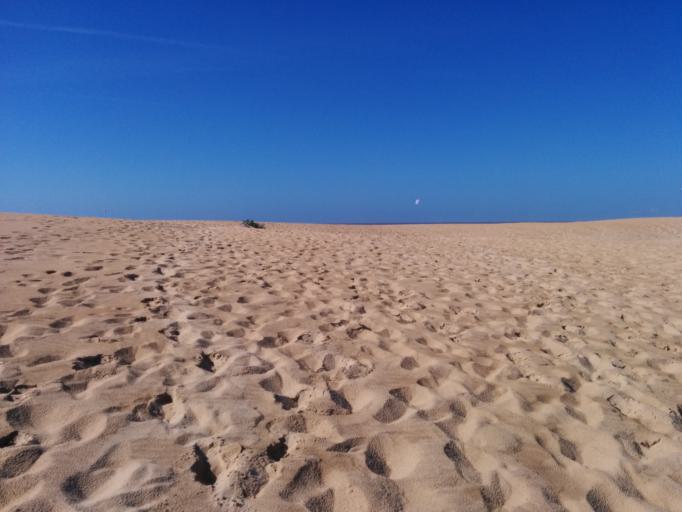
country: PT
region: Faro
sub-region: Vila do Bispo
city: Vila do Bispo
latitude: 37.1969
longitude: -8.9021
